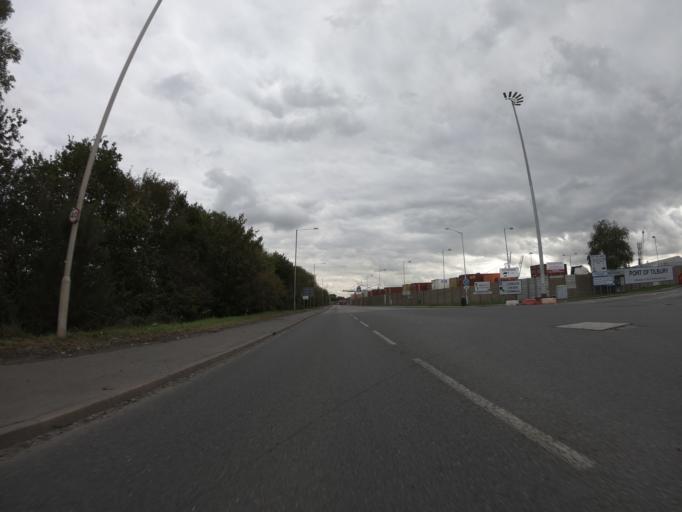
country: GB
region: England
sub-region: Borough of Thurrock
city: Tilbury
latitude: 51.4639
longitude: 0.3503
